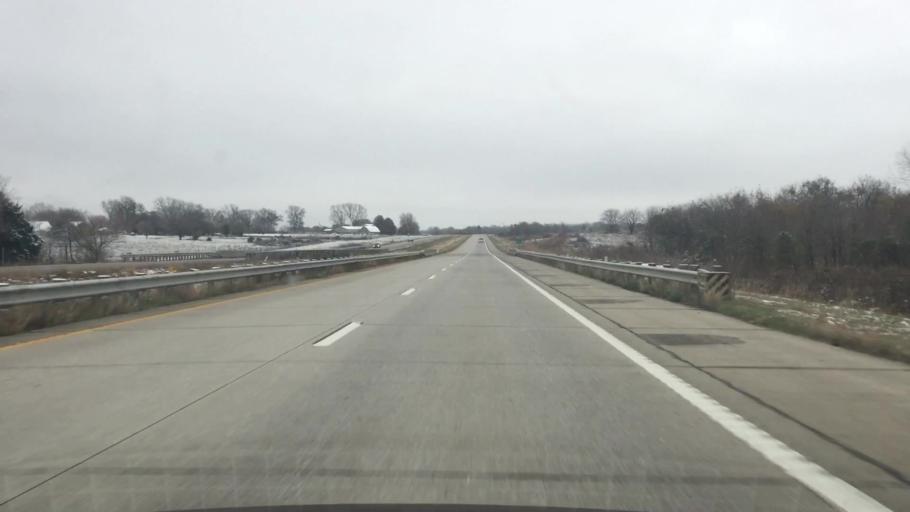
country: US
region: Missouri
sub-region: Saint Clair County
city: Osceola
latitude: 38.1958
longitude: -93.7448
